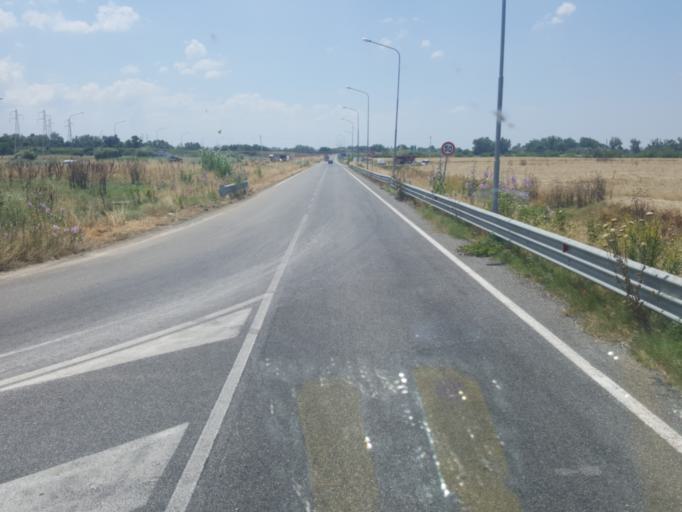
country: IT
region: Latium
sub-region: Citta metropolitana di Roma Capitale
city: Fiano Romano
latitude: 42.1589
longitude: 12.6431
